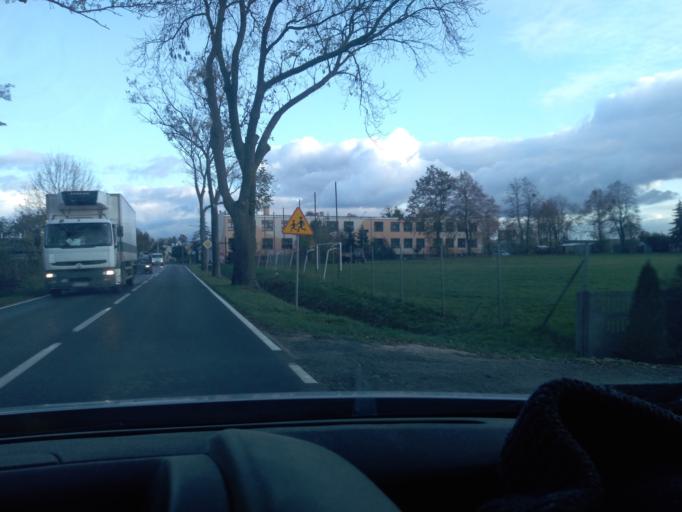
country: PL
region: Greater Poland Voivodeship
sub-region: Powiat poznanski
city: Murowana Goslina
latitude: 52.6299
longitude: 16.9757
